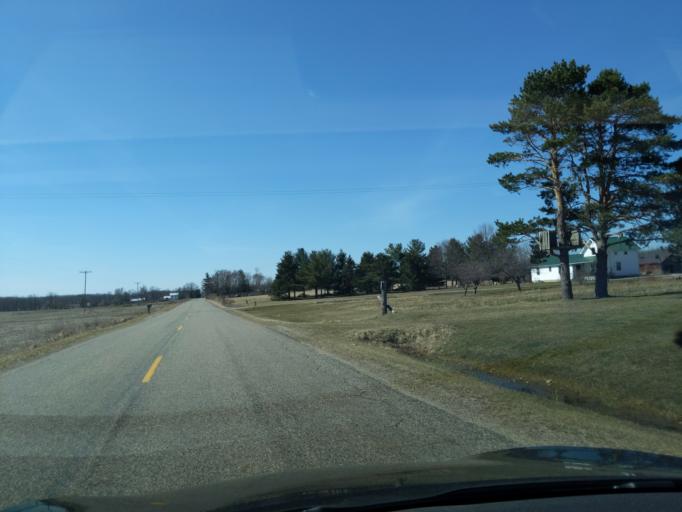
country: US
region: Michigan
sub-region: Ionia County
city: Lake Odessa
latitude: 42.7125
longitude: -85.0658
